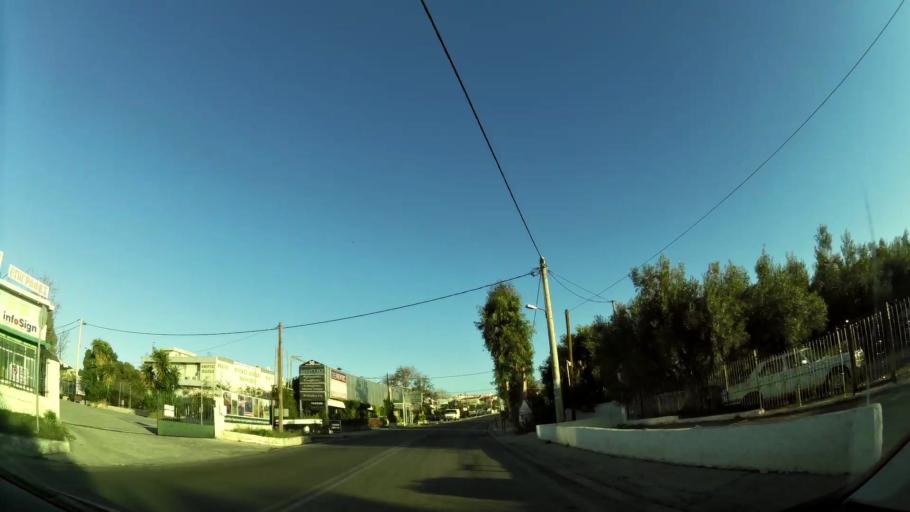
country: GR
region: Attica
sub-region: Nomarchia Anatolikis Attikis
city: Pallini
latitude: 37.9978
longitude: 23.8802
